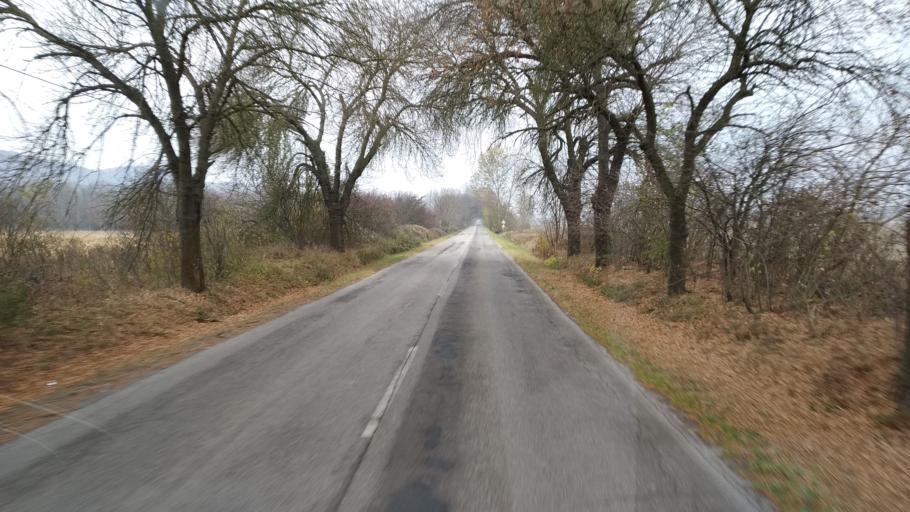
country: HU
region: Pest
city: Dunabogdany
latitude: 47.8002
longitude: 19.0434
